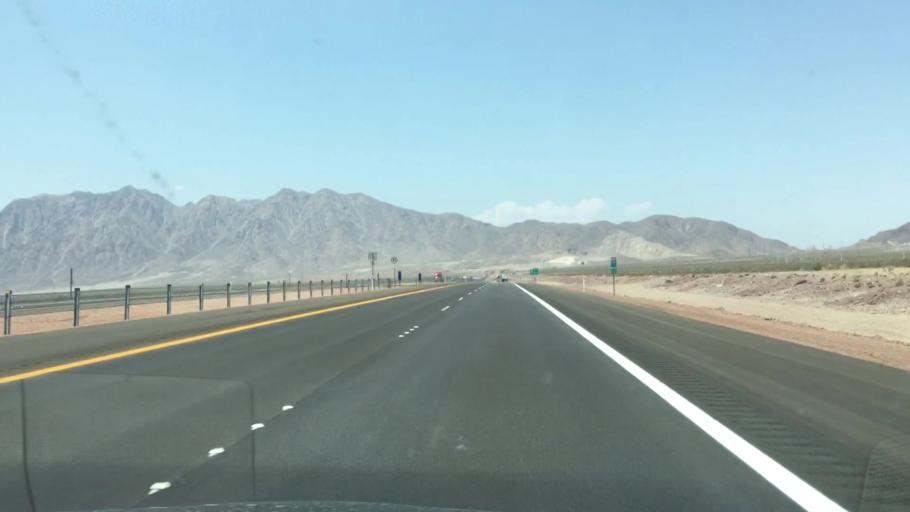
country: US
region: Nevada
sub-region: Clark County
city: Boulder City
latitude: 35.9405
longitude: -114.8761
